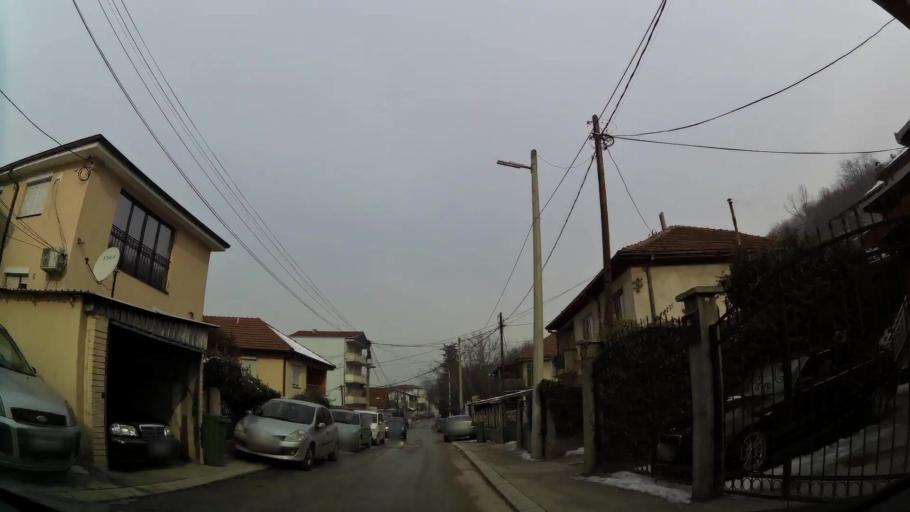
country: MK
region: Cair
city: Cair
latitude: 42.0094
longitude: 21.4468
